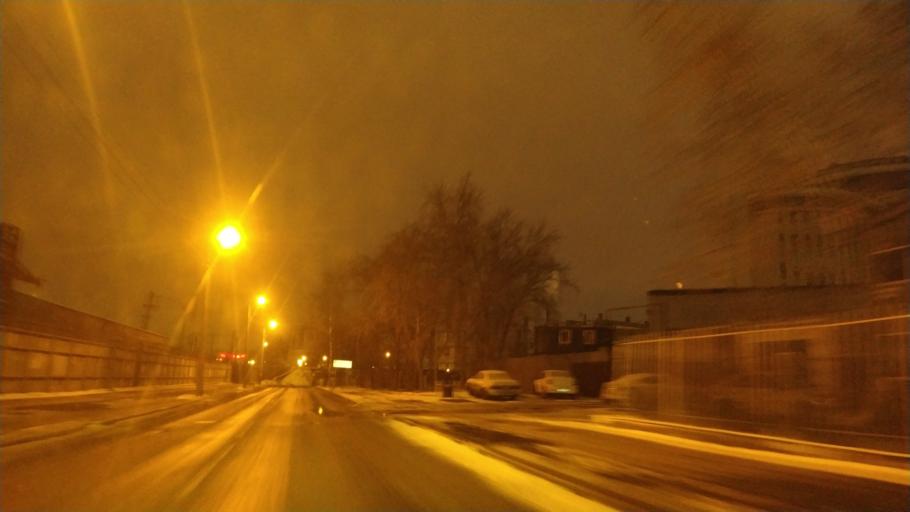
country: RU
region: St.-Petersburg
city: Kupchino
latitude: 59.8830
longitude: 30.3282
